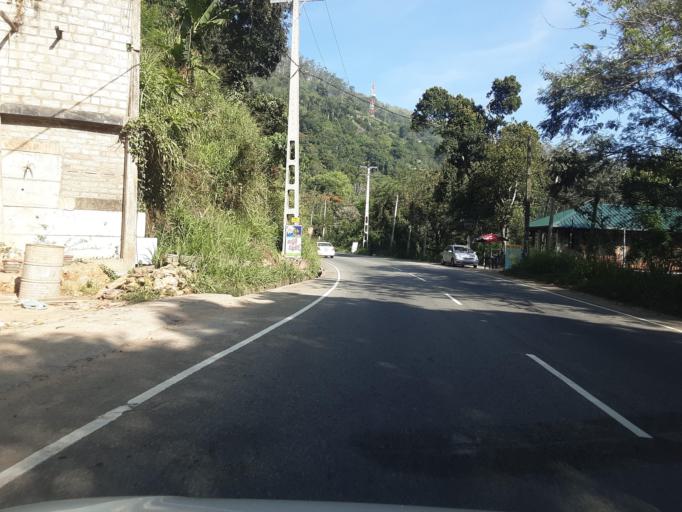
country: LK
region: Uva
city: Badulla
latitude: 6.9778
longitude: 81.0446
